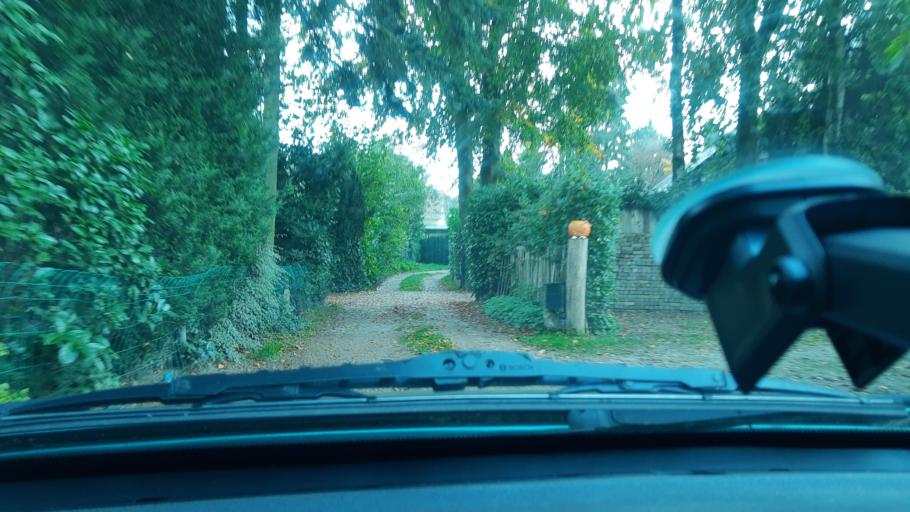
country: NL
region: North Brabant
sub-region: Gemeente Boxmeer
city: Boxmeer
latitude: 51.6546
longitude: 5.9948
